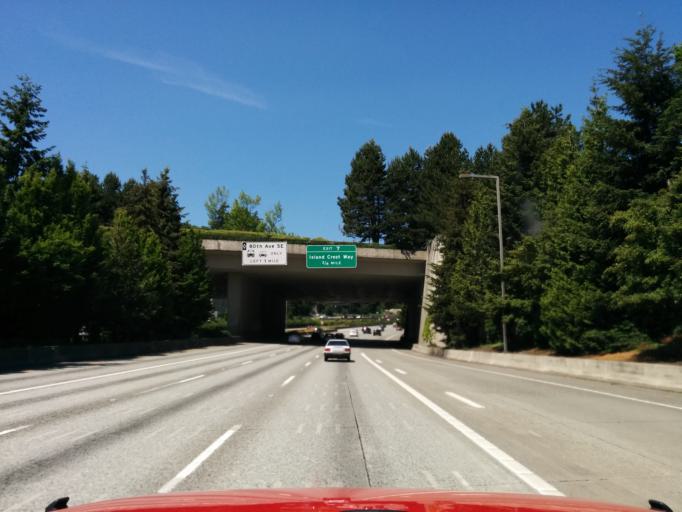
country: US
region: Washington
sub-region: King County
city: Mercer Island
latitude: 47.5789
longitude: -122.2114
